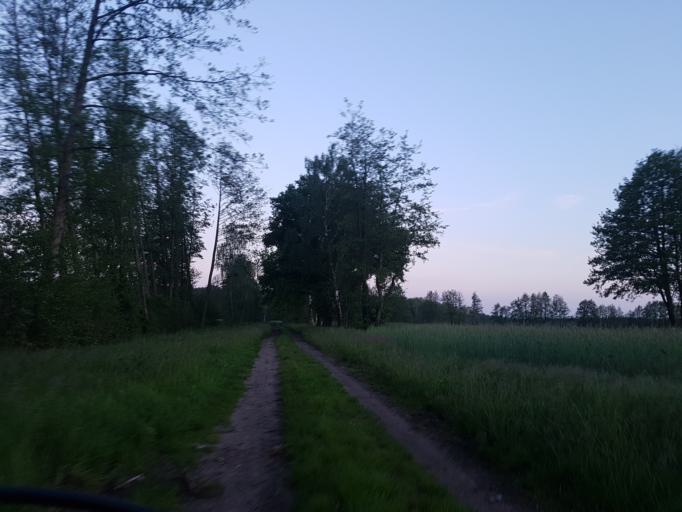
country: DE
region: Brandenburg
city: Schilda
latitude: 51.5690
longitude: 13.3736
